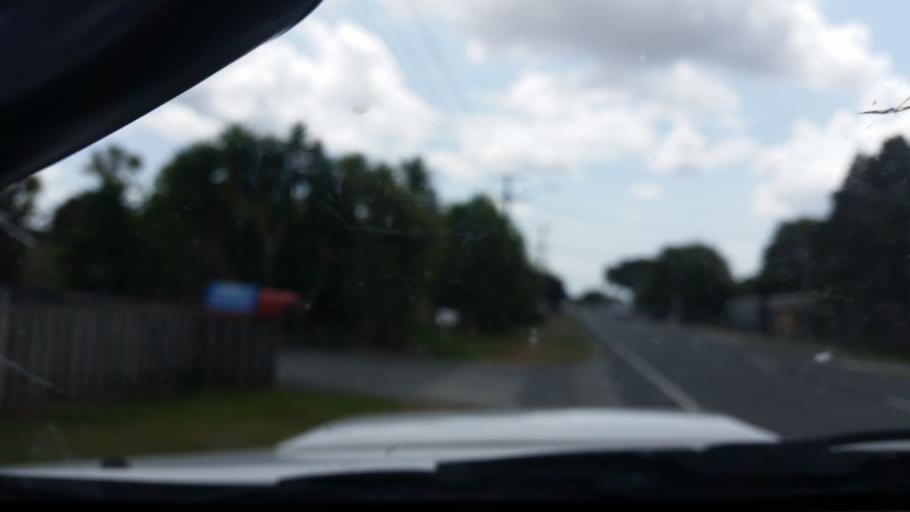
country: NZ
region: Auckland
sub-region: Auckland
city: Wellsford
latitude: -36.1269
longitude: 174.5719
